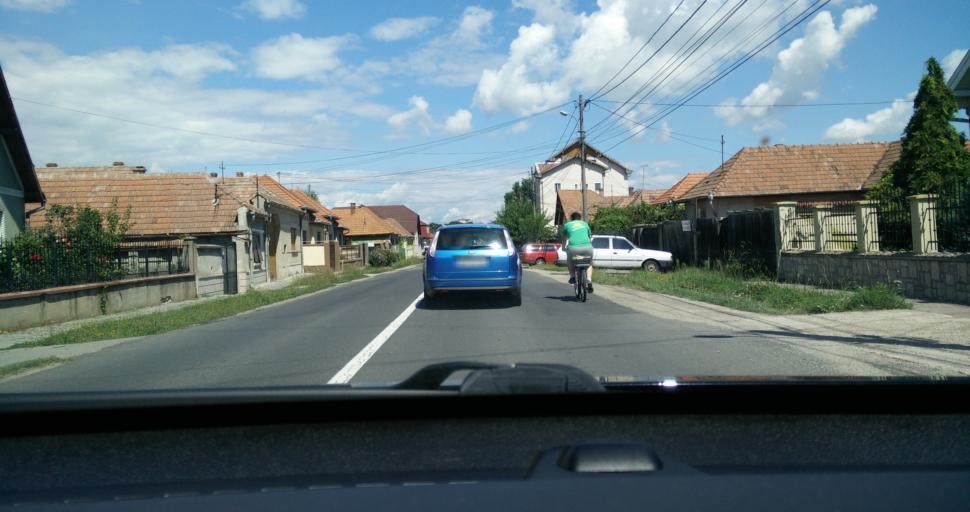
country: RO
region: Alba
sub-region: Municipiul Sebes
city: Sebes
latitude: 45.9443
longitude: 23.5640
